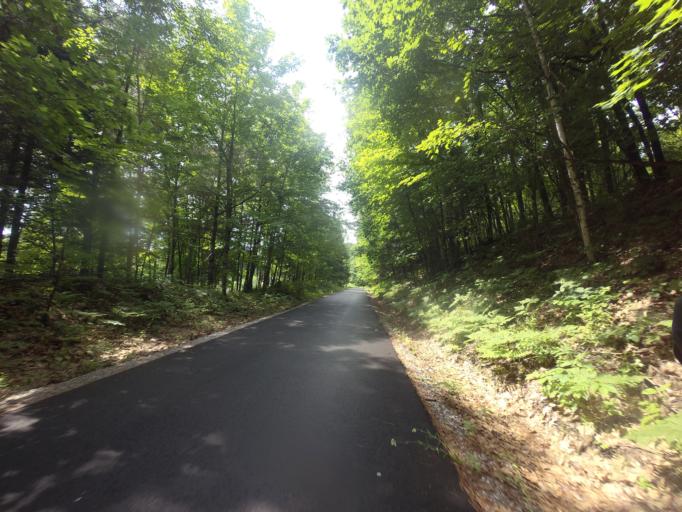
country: CA
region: Quebec
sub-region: Outaouais
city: Maniwaki
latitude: 46.1363
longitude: -76.0359
